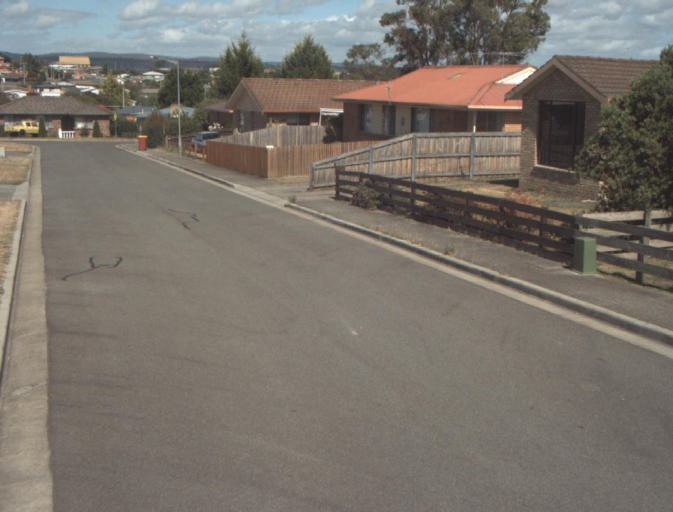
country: AU
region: Tasmania
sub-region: Launceston
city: Newstead
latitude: -41.4198
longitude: 147.1814
